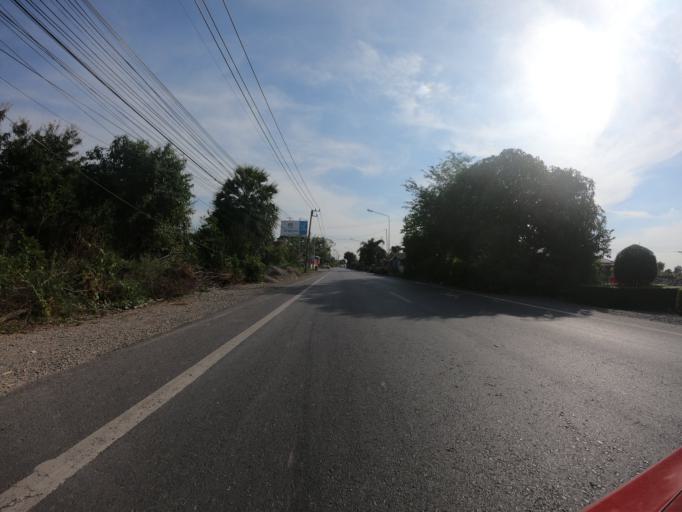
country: TH
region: Pathum Thani
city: Thanyaburi
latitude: 13.9842
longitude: 100.7295
